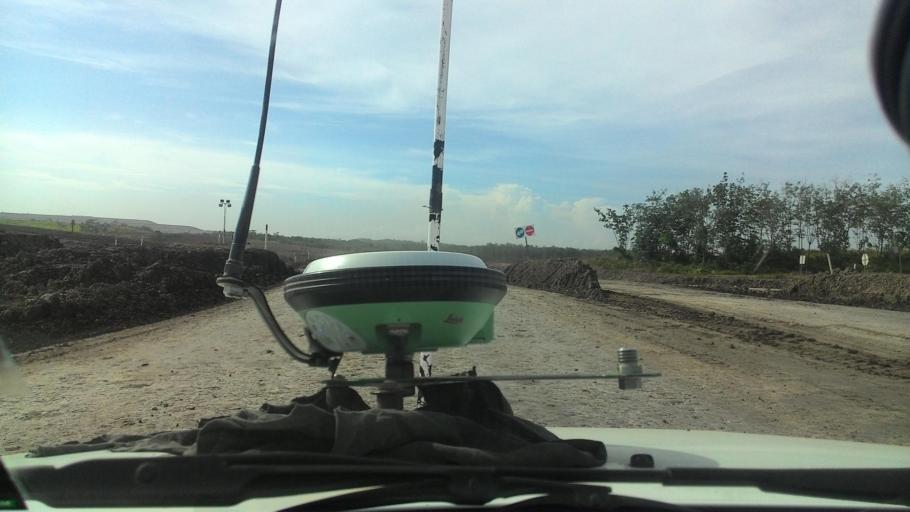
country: ID
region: South Kalimantan
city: Tanta
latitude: -2.1859
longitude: 115.4726
